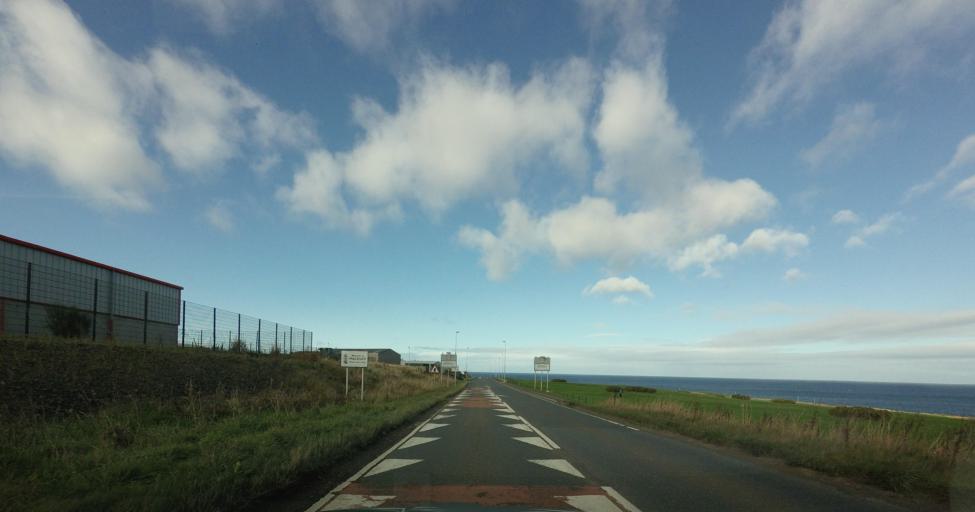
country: GB
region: Scotland
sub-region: Aberdeenshire
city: Macduff
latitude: 57.6673
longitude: -2.4761
